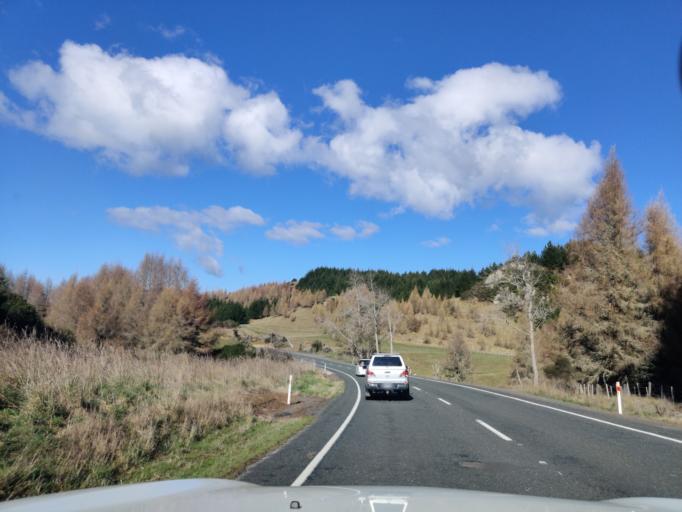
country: NZ
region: Waikato
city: Turangi
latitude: -38.6845
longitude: 175.6833
